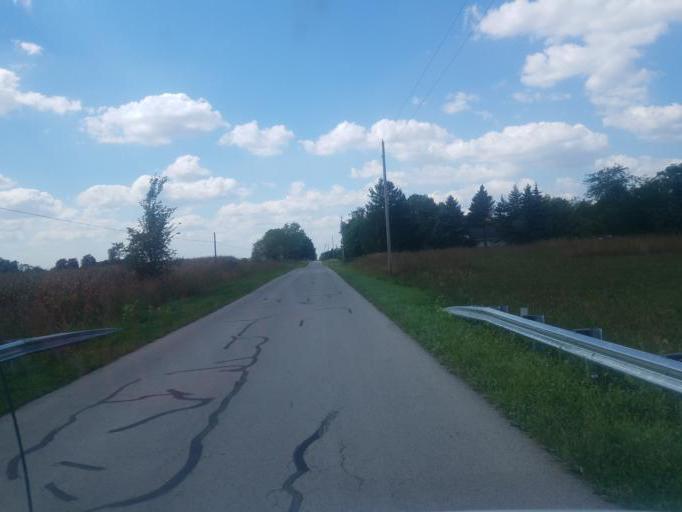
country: US
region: Ohio
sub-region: Allen County
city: Lima
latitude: 40.6515
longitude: -83.9649
